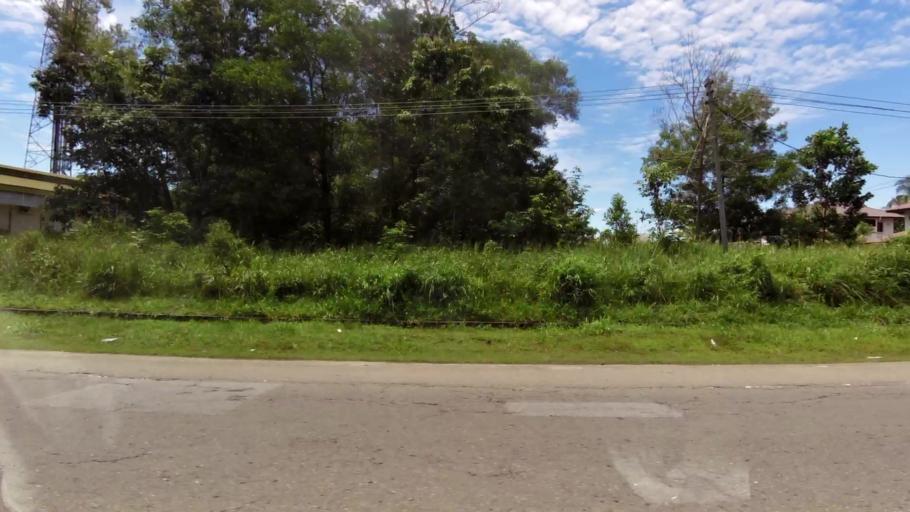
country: BN
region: Brunei and Muara
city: Bandar Seri Begawan
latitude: 5.0004
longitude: 115.0254
